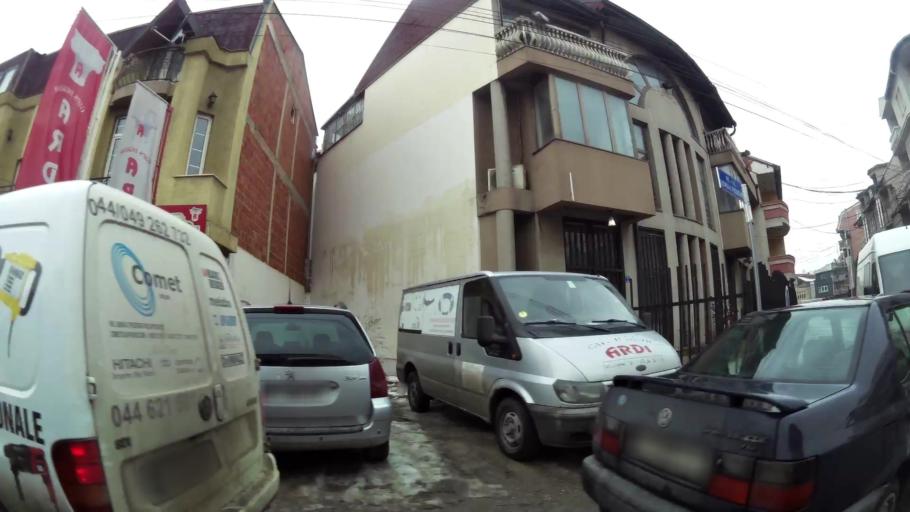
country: XK
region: Pristina
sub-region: Komuna e Prishtines
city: Pristina
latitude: 42.6674
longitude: 21.1609
